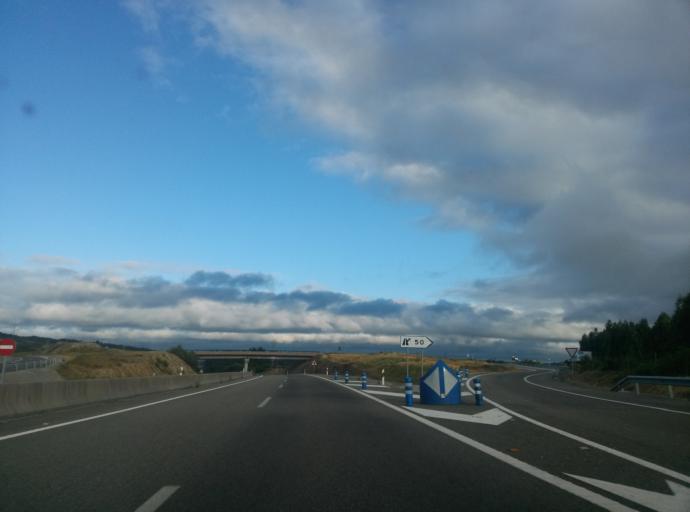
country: ES
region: Galicia
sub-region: Provincia de Lugo
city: Vilalba
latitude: 43.3545
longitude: -7.7472
